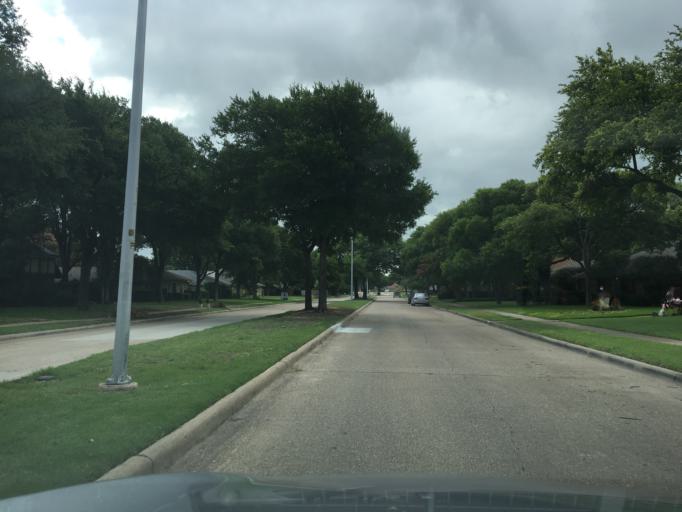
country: US
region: Texas
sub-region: Dallas County
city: Richardson
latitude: 32.9398
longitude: -96.7176
